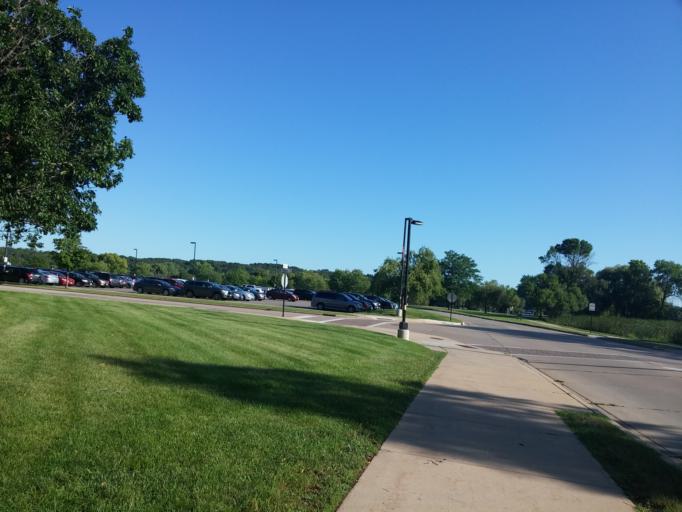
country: US
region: Wisconsin
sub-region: Dane County
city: Shorewood Hills
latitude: 43.0786
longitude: -89.4252
